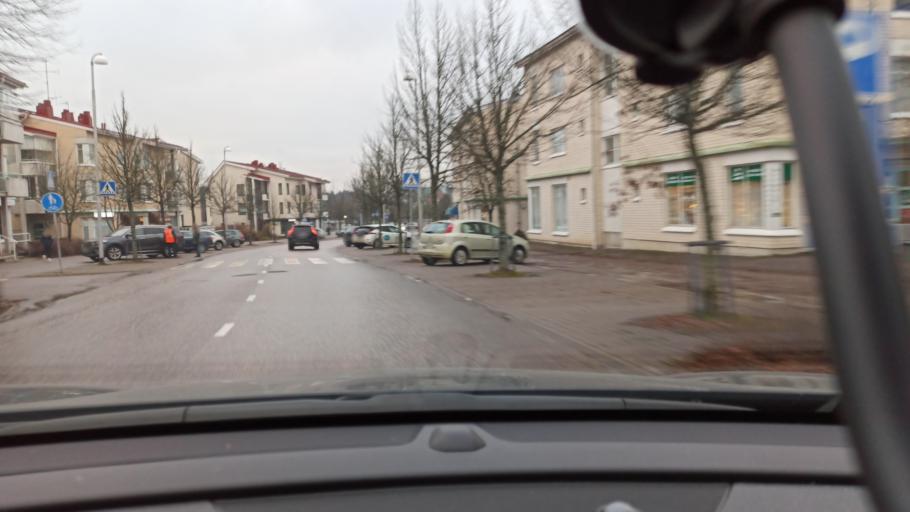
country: FI
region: Uusimaa
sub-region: Helsinki
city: Kirkkonummi
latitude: 60.1278
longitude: 24.4357
